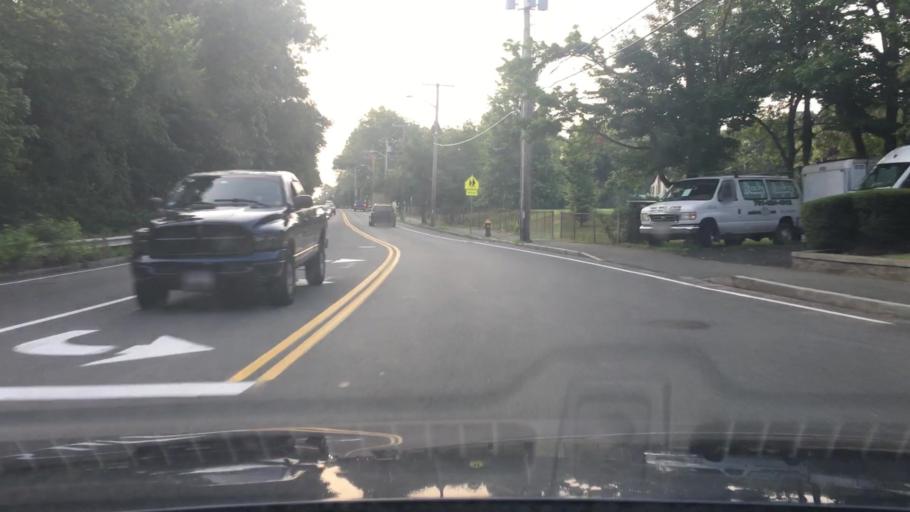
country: US
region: Massachusetts
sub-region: Essex County
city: Saugus
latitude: 42.4771
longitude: -71.0021
